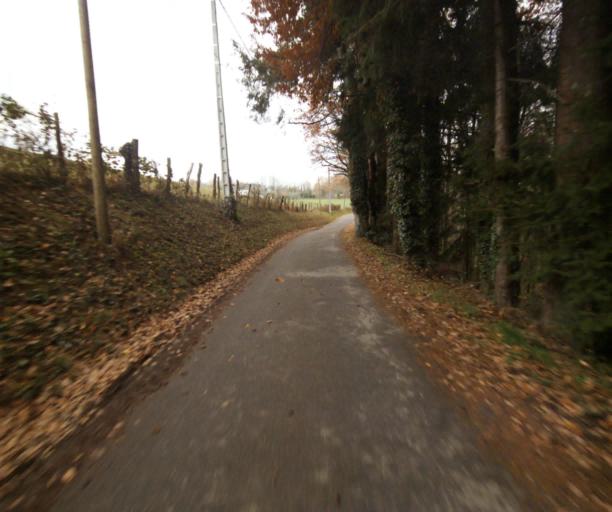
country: FR
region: Limousin
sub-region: Departement de la Correze
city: Laguenne
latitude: 45.2272
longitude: 1.7829
